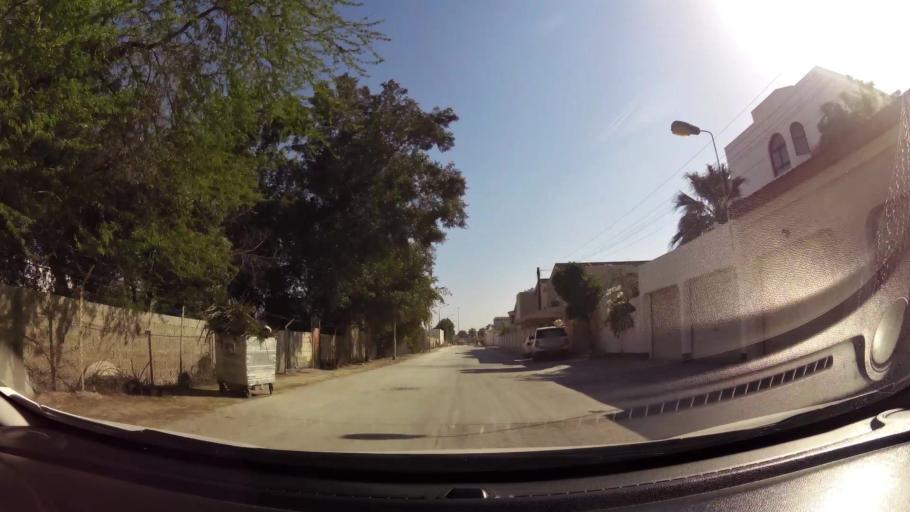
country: BH
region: Manama
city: Manama
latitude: 26.2081
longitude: 50.5713
